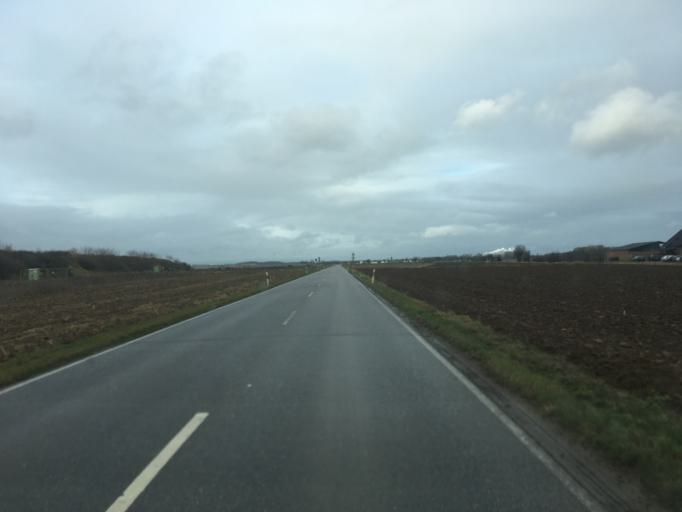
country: DE
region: North Rhine-Westphalia
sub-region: Regierungsbezirk Koln
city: Niederzier
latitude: 50.8573
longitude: 6.4217
